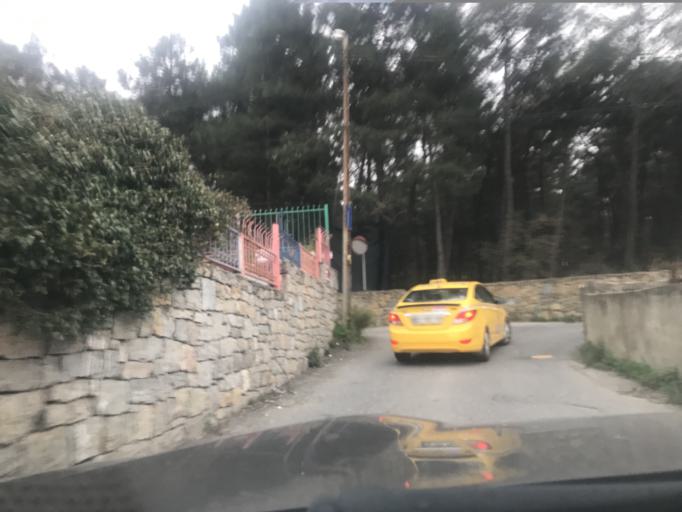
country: TR
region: Istanbul
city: Umraniye
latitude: 41.0284
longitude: 29.1325
